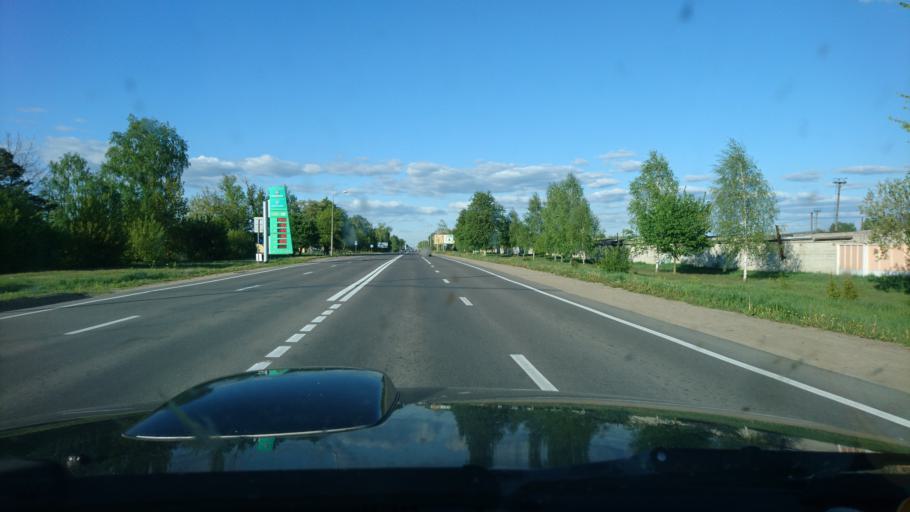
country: BY
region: Brest
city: Ivatsevichy
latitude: 52.7006
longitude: 25.3203
